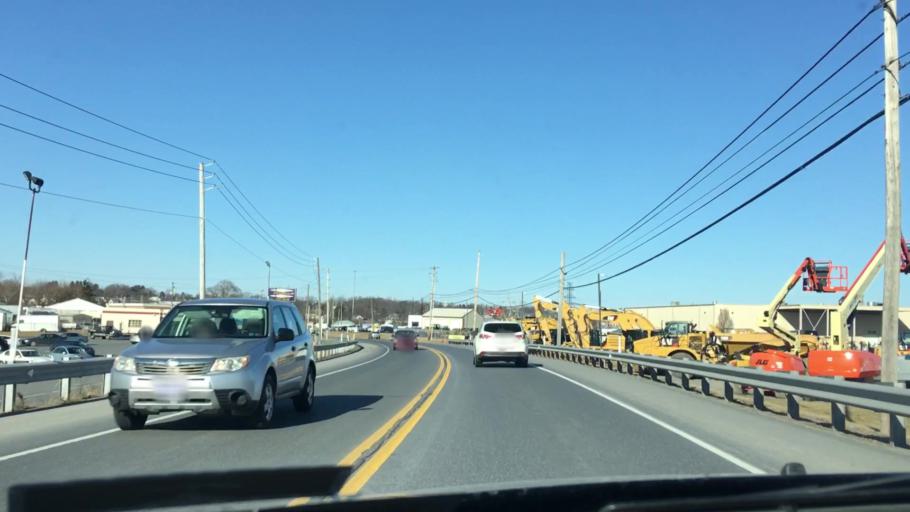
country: US
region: Pennsylvania
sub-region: Lancaster County
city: Brownstown
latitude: 40.1348
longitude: -76.2121
